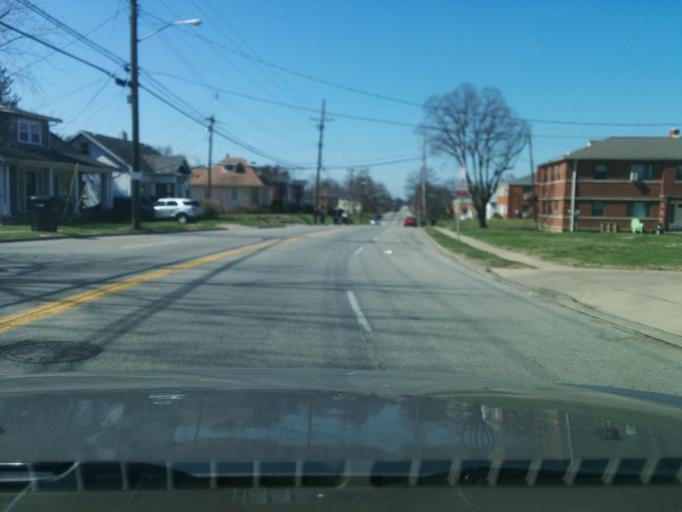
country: US
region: Ohio
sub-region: Hamilton County
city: Monfort Heights
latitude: 39.1891
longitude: -84.5740
